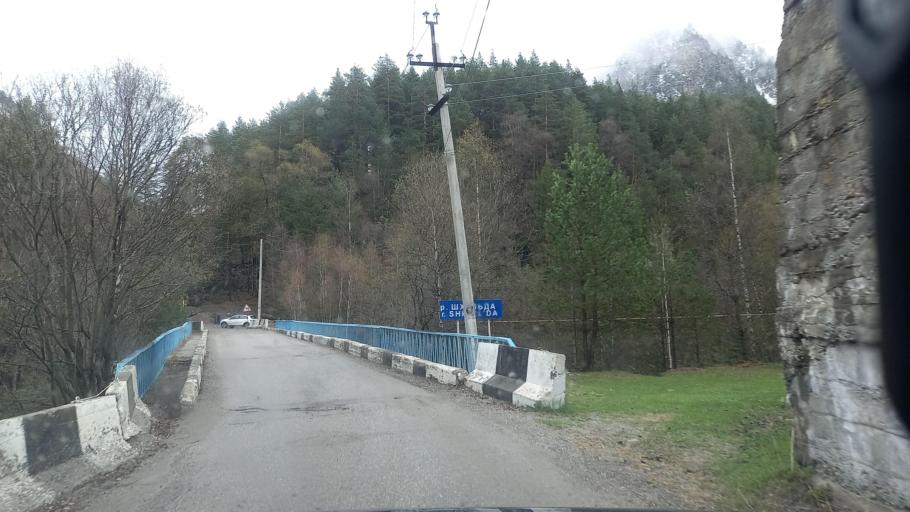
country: RU
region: Kabardino-Balkariya
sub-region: El'brusskiy Rayon
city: El'brus
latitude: 43.2290
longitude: 42.6544
